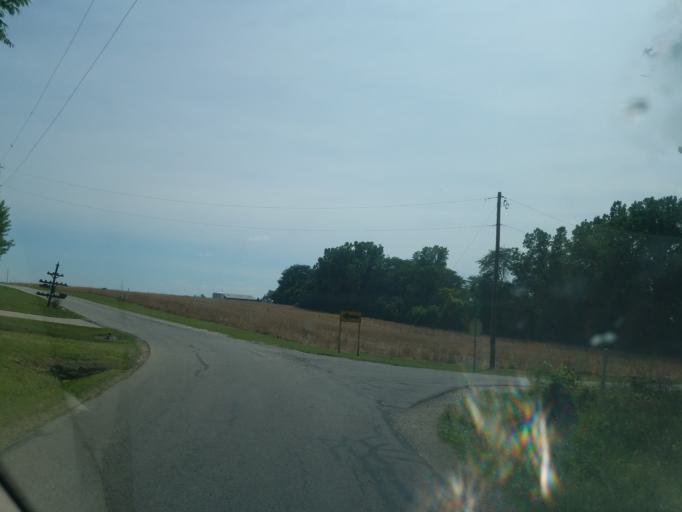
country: US
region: Ohio
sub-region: Seneca County
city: Tiffin
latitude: 41.1089
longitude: -83.2687
